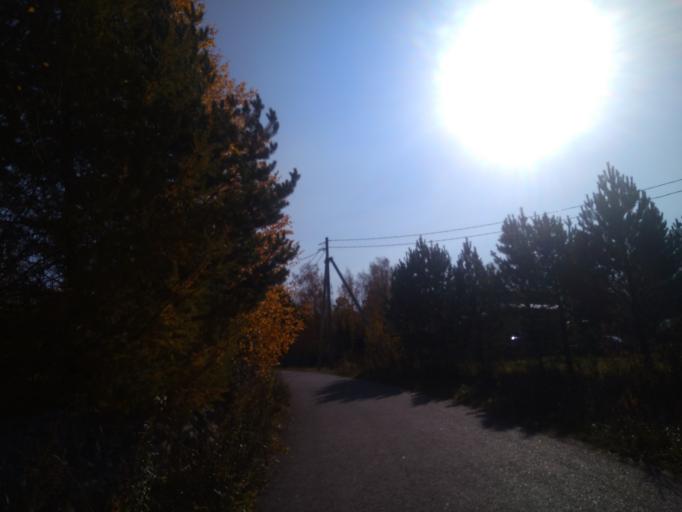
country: RU
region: Sverdlovsk
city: Mikhaylovsk
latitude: 56.5245
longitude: 59.2297
